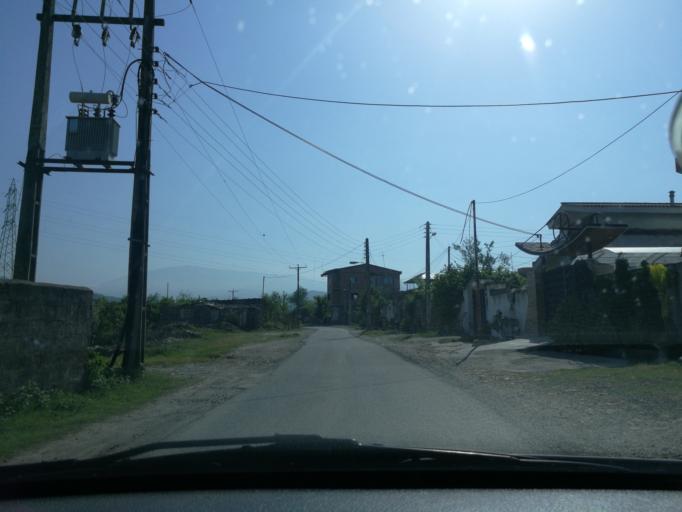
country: IR
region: Mazandaran
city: Chalus
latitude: 36.6612
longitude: 51.4377
